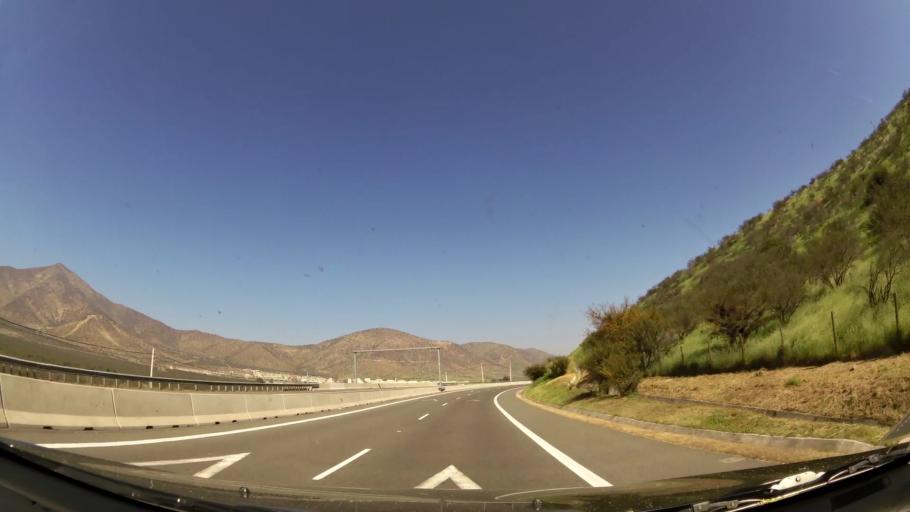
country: CL
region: Santiago Metropolitan
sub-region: Provincia de Chacabuco
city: Chicureo Abajo
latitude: -33.3133
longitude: -70.6379
